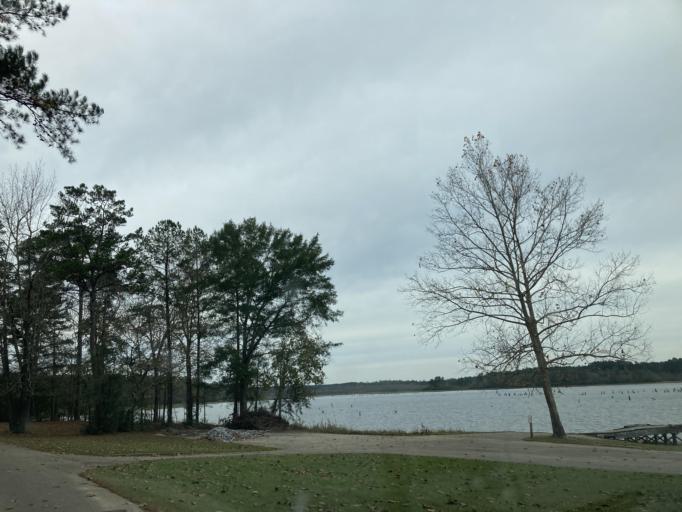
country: US
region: Mississippi
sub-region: Lamar County
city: Lumberton
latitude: 31.0836
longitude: -89.4964
